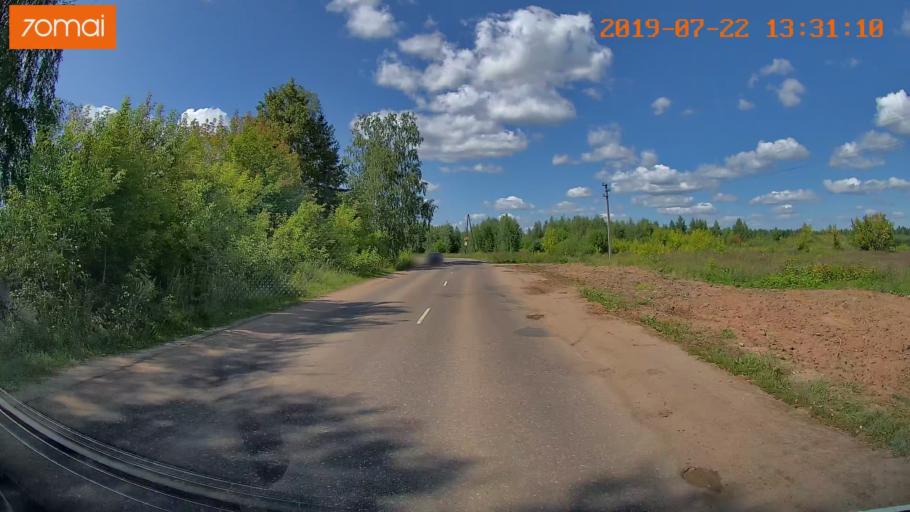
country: RU
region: Ivanovo
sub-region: Gorod Ivanovo
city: Ivanovo
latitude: 57.0566
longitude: 40.9195
